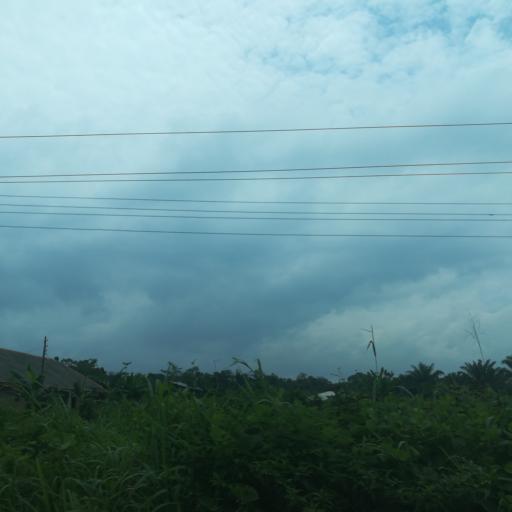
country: NG
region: Lagos
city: Ejirin
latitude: 6.6472
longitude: 3.7798
